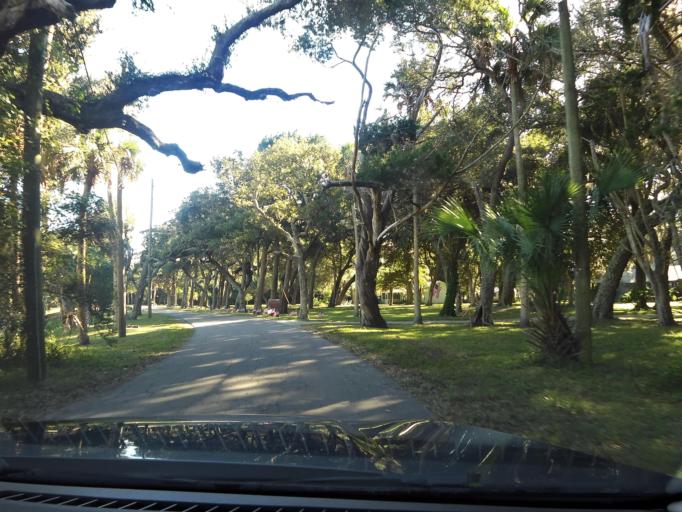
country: US
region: Florida
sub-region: Duval County
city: Atlantic Beach
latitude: 30.4238
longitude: -81.4280
